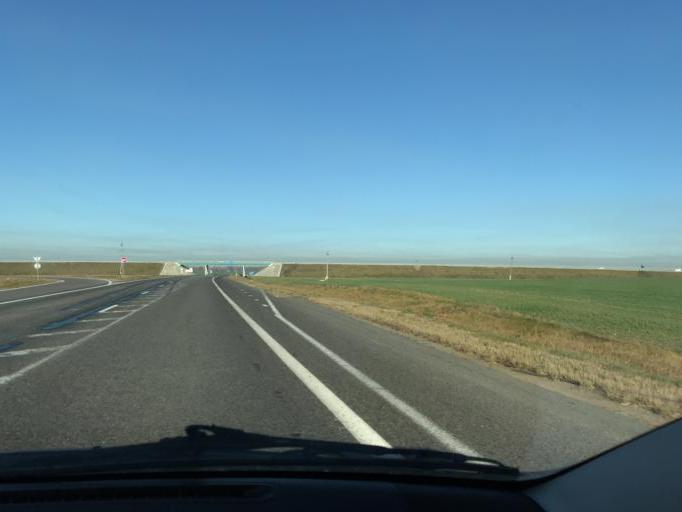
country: BY
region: Vitebsk
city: Vitebsk
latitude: 55.1083
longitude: 30.1089
